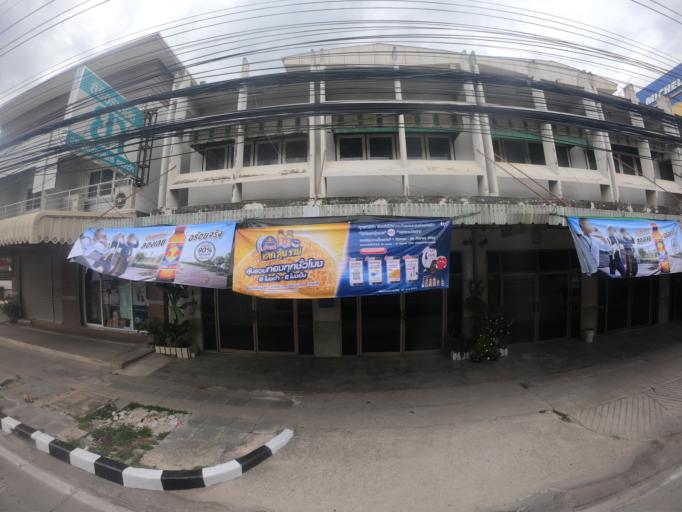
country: TH
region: Nakhon Ratchasima
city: Nakhon Ratchasima
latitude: 14.9558
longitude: 102.1208
